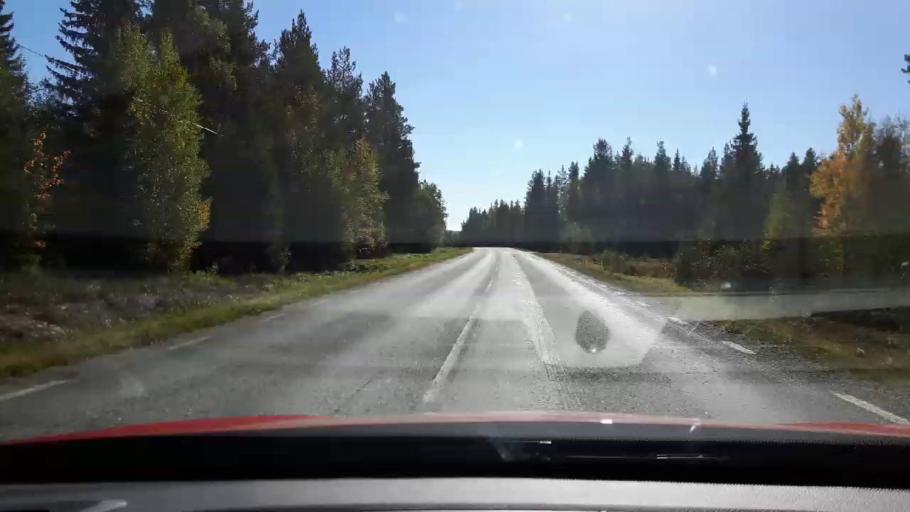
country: SE
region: Jaemtland
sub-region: Harjedalens Kommun
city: Sveg
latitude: 62.4337
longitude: 13.8829
